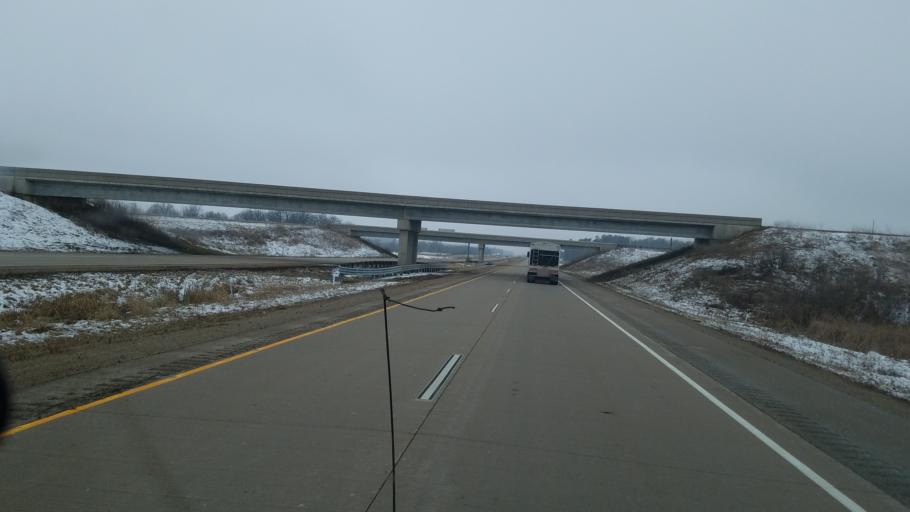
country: US
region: Wisconsin
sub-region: Winnebago County
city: Winneconne
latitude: 44.2343
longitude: -88.7374
